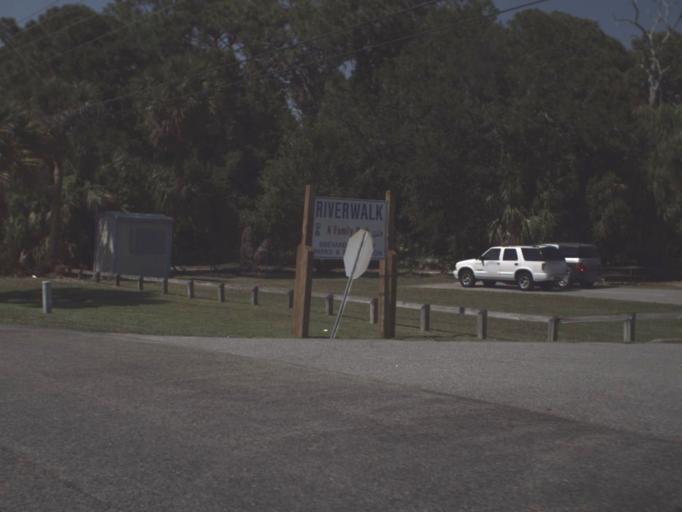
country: US
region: Florida
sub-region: Brevard County
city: Rockledge
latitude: 28.2680
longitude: -80.6903
